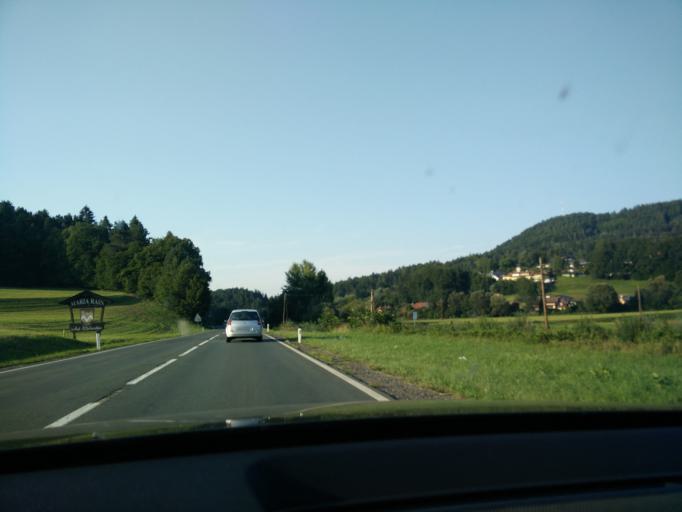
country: AT
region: Carinthia
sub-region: Politischer Bezirk Klagenfurt Land
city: Maria Rain
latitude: 46.5679
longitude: 14.2852
